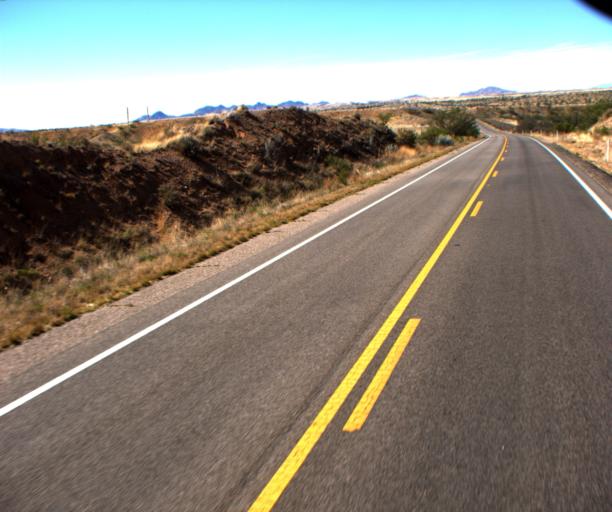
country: US
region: Arizona
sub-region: Pima County
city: Corona de Tucson
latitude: 31.7258
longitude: -110.6570
